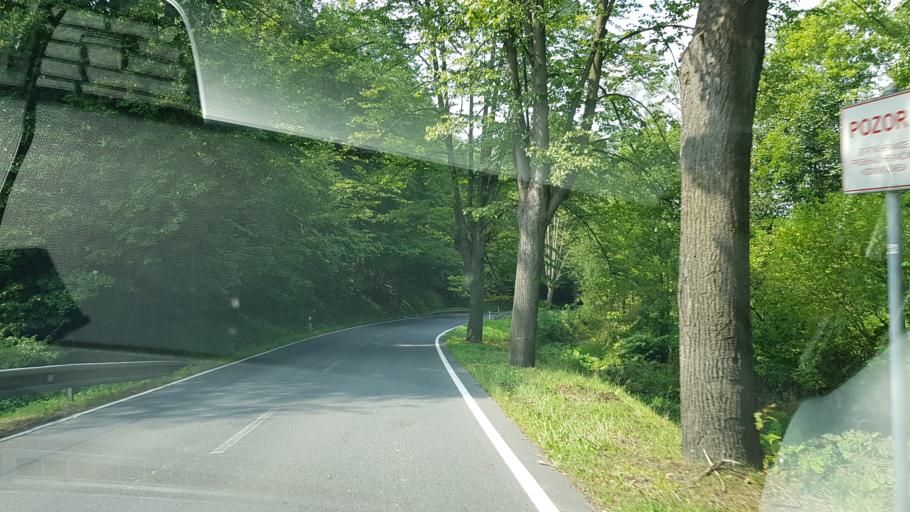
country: CZ
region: Olomoucky
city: Mikulovice
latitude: 50.2637
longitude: 17.3506
